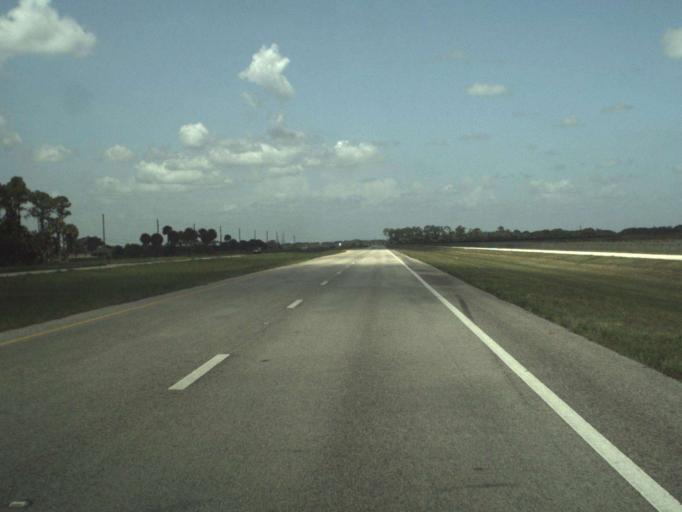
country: US
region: Florida
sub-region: Saint Lucie County
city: Fort Pierce South
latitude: 27.3679
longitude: -80.5174
